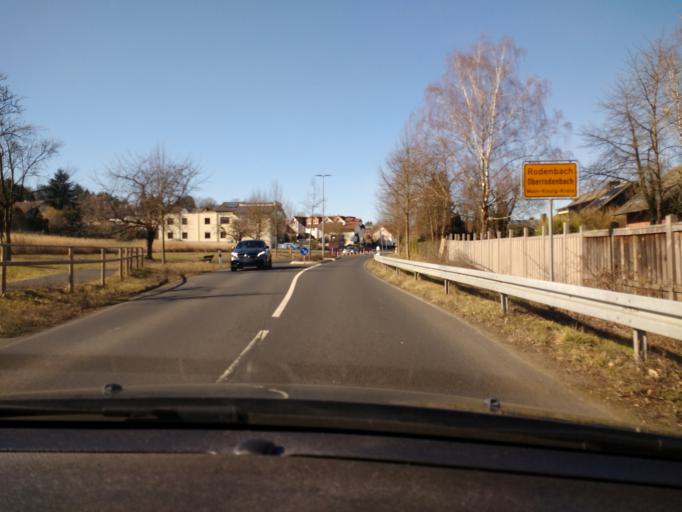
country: DE
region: Hesse
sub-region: Regierungsbezirk Darmstadt
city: Rodenbach
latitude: 50.1338
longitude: 9.0658
